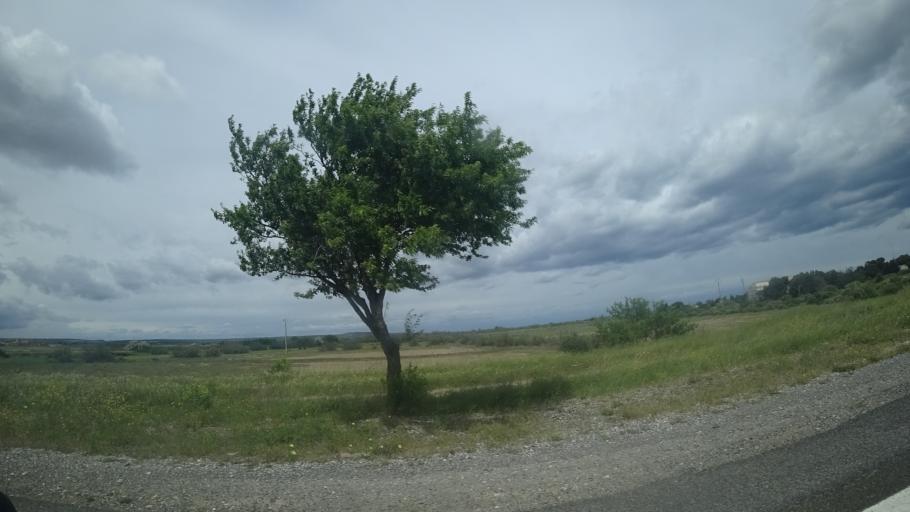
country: FR
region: Languedoc-Roussillon
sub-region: Departement de l'Aude
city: Leucate
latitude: 42.9321
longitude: 3.0092
